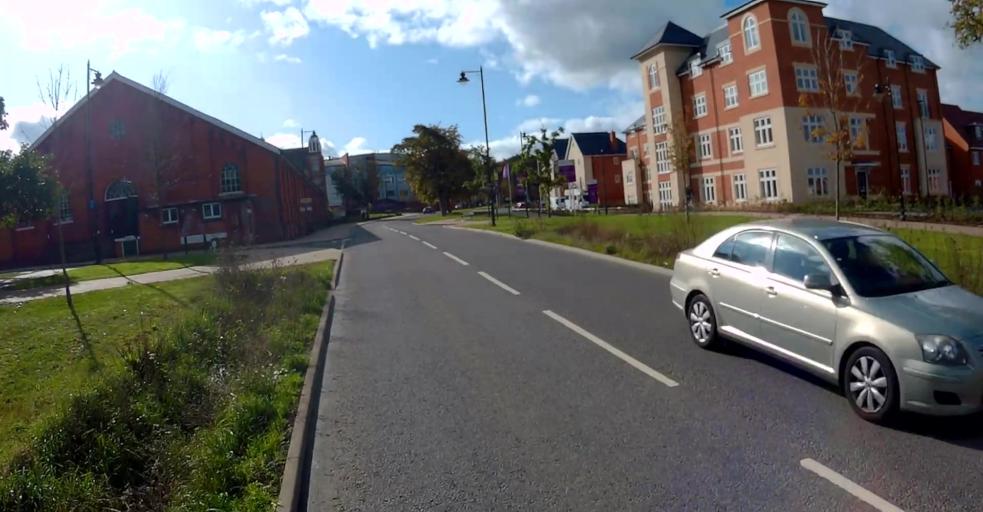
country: GB
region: England
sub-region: Hampshire
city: Aldershot
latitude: 51.2558
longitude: -0.7645
